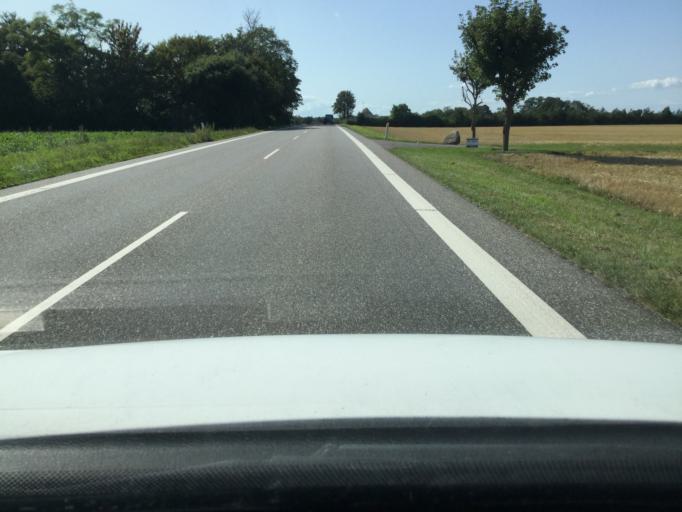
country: DK
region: Zealand
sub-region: Lolland Kommune
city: Nakskov
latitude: 54.8028
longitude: 11.2617
